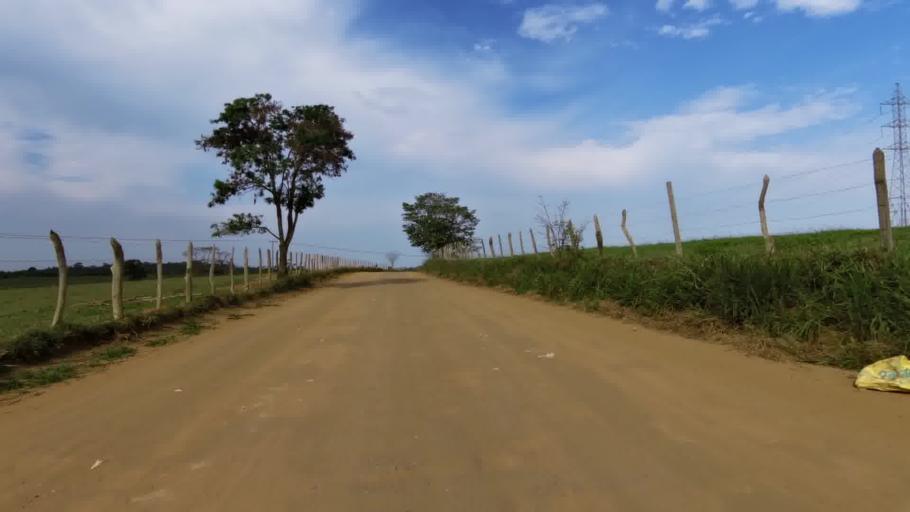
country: BR
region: Espirito Santo
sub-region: Piuma
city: Piuma
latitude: -20.8285
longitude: -40.7425
